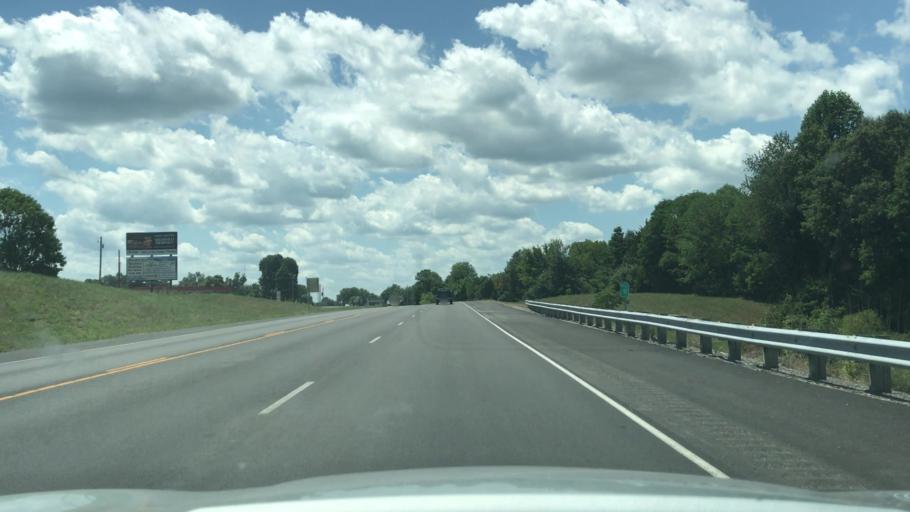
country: US
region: Kentucky
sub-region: Muhlenberg County
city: Greenville
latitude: 37.2022
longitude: -87.2021
